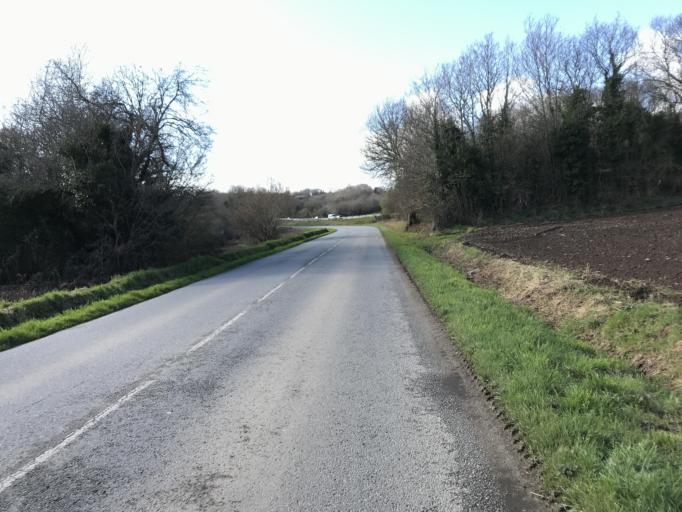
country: FR
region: Brittany
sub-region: Departement du Finistere
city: Loperhet
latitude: 48.3820
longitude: -4.3327
